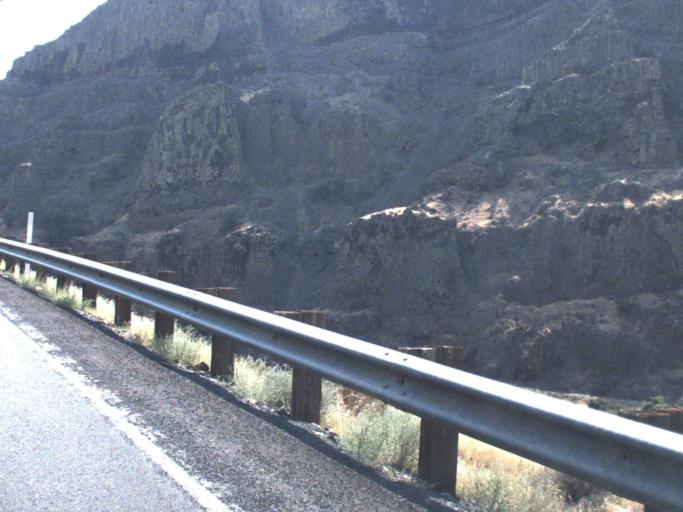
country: US
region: Washington
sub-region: Yakima County
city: Selah
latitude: 46.7302
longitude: -120.4528
